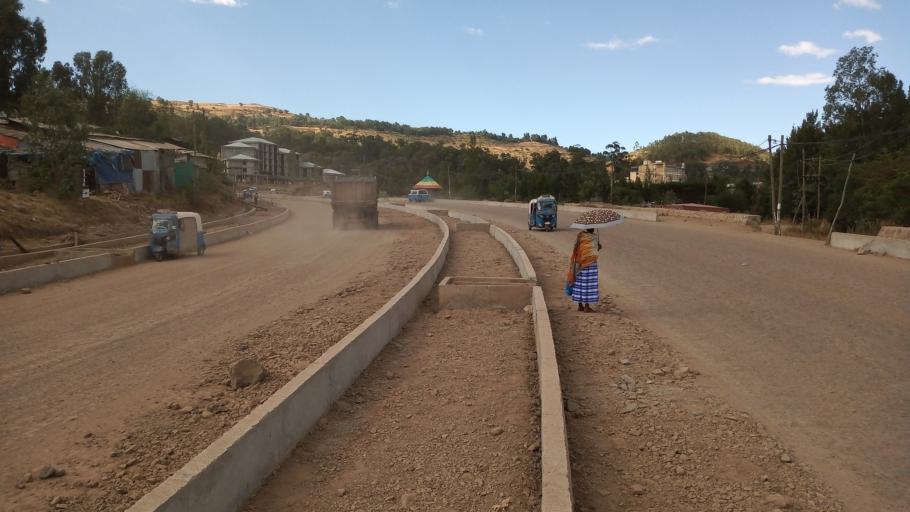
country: ET
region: Amhara
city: Gondar
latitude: 12.5697
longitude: 37.4339
